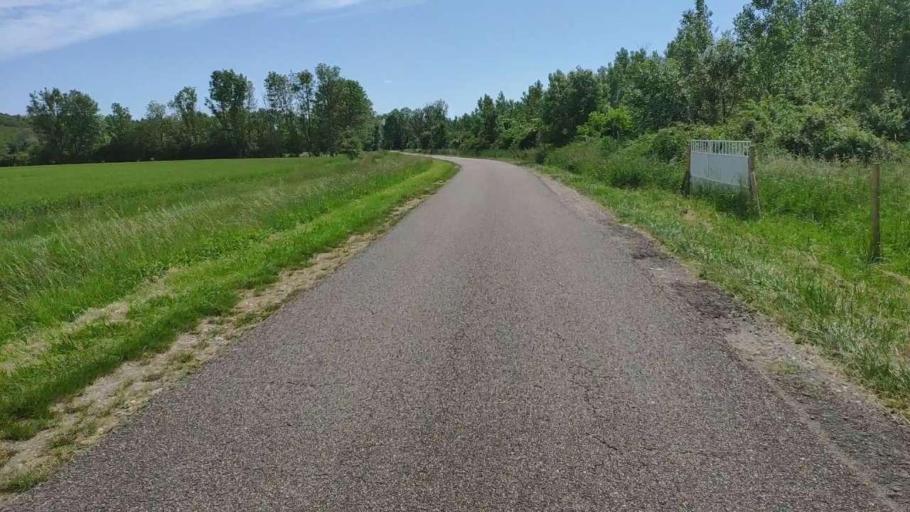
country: FR
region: Franche-Comte
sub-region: Departement du Jura
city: Bletterans
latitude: 46.7254
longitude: 5.4775
